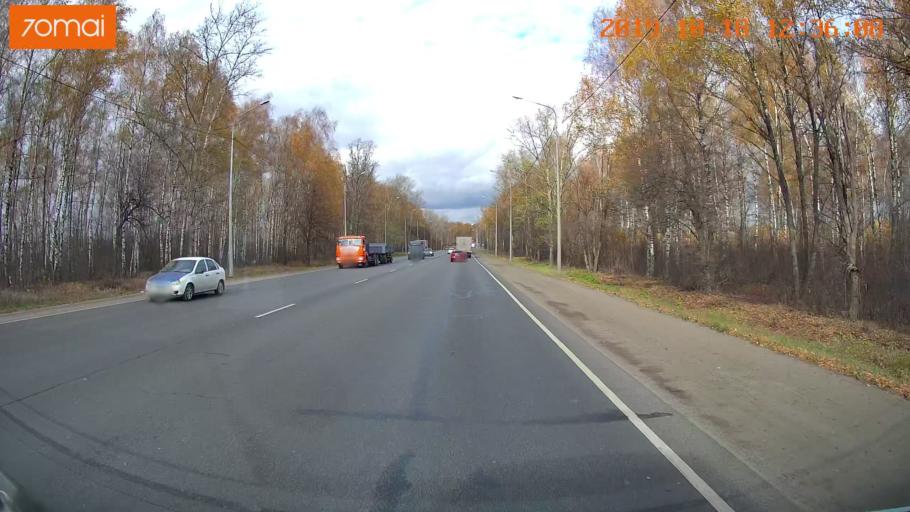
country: RU
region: Rjazan
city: Ryazan'
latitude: 54.6319
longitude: 39.6344
